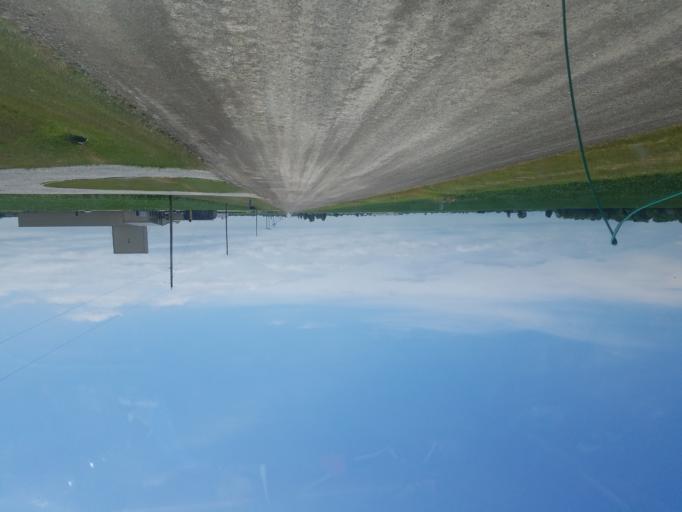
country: US
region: Indiana
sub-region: Allen County
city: Woodburn
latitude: 41.1636
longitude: -84.8490
